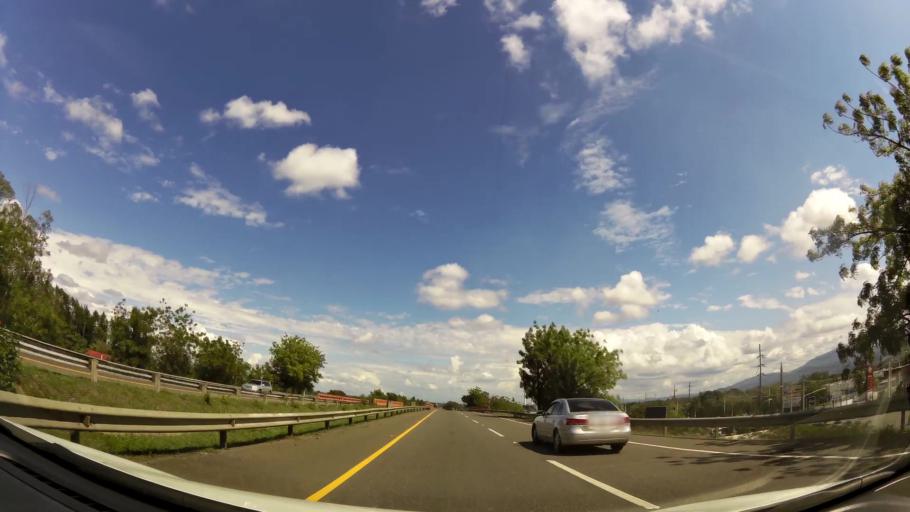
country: DO
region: La Vega
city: Concepcion de La Vega
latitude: 19.2505
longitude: -70.5558
